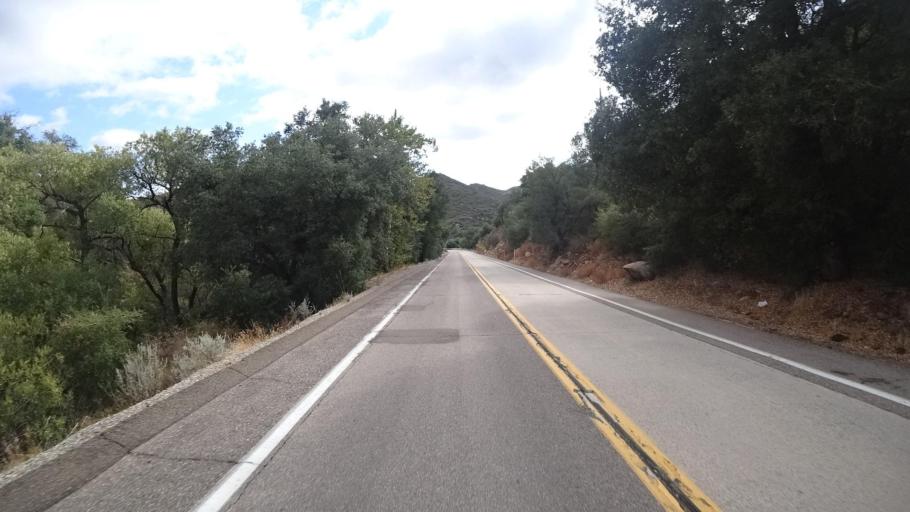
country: US
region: California
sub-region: San Diego County
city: Pine Valley
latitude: 32.7902
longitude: -116.4970
